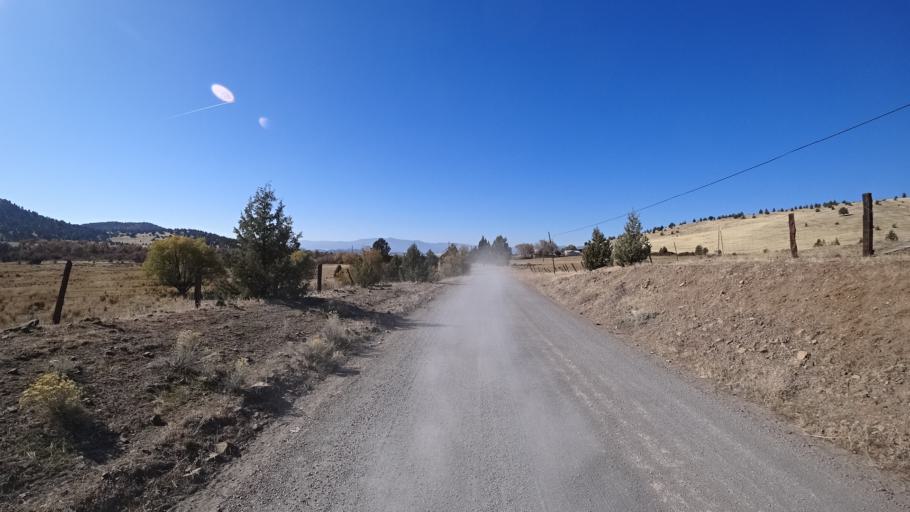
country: US
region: California
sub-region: Siskiyou County
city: Montague
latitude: 41.7296
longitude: -122.3599
